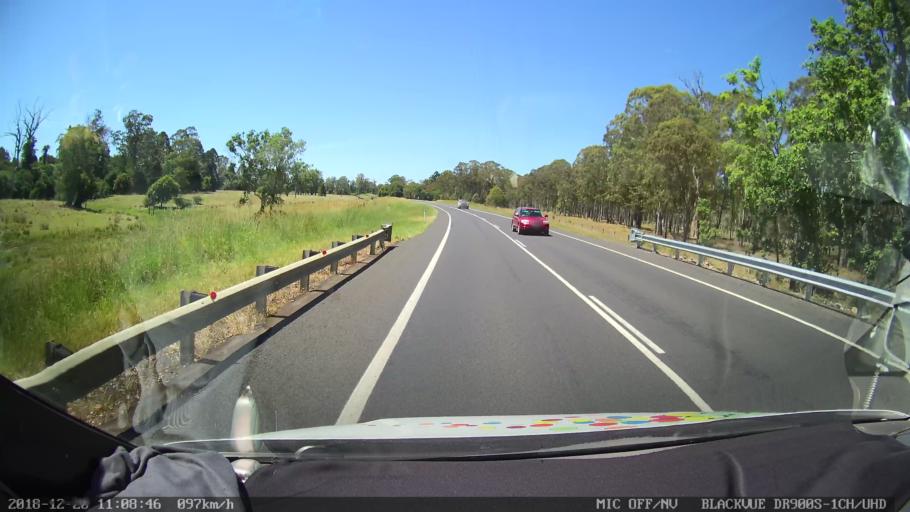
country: AU
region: New South Wales
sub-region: Richmond Valley
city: Casino
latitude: -28.9266
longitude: 153.0047
